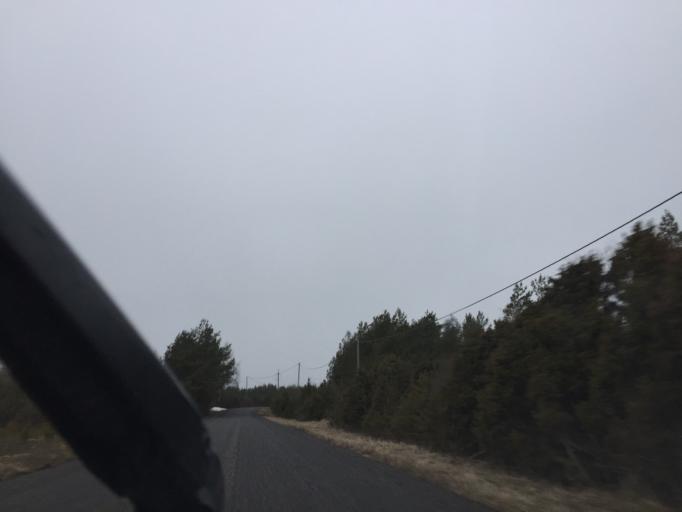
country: EE
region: Laeaene
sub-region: Lihula vald
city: Lihula
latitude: 58.6573
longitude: 23.5914
